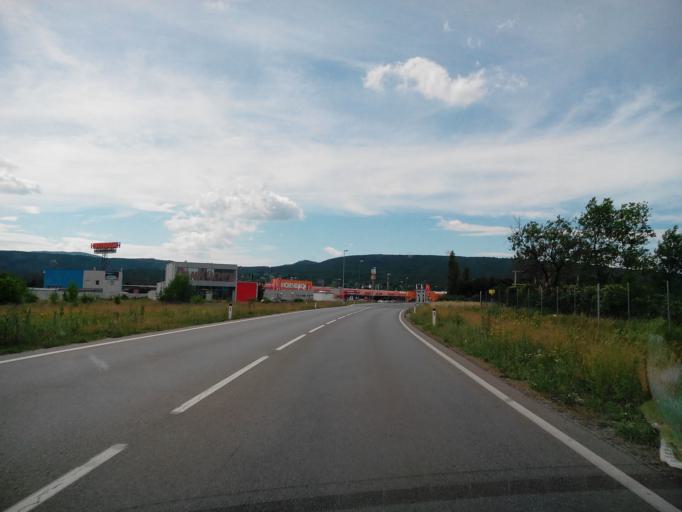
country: AT
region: Lower Austria
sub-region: Politischer Bezirk Wiener Neustadt
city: Theresienfeld
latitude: 47.8299
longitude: 16.1893
